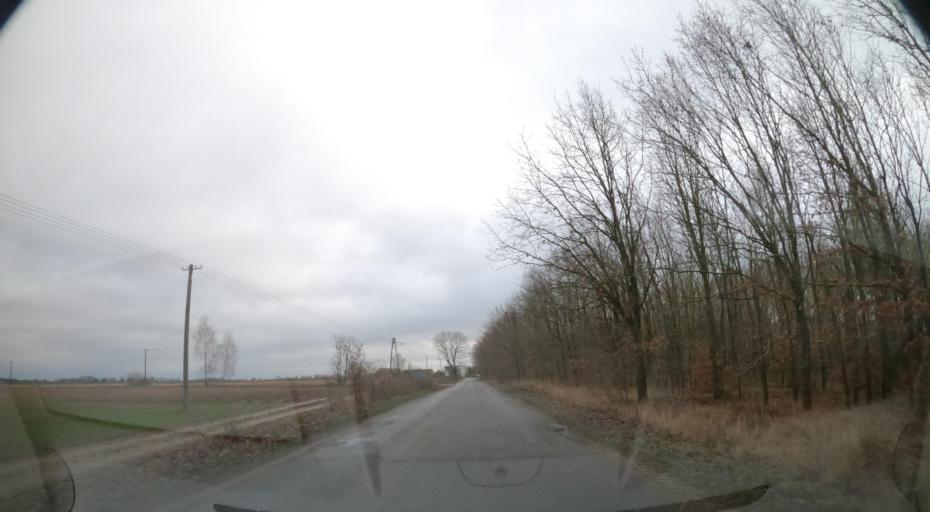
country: PL
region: Greater Poland Voivodeship
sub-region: Powiat pilski
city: Lobzenica
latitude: 53.2396
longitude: 17.3024
